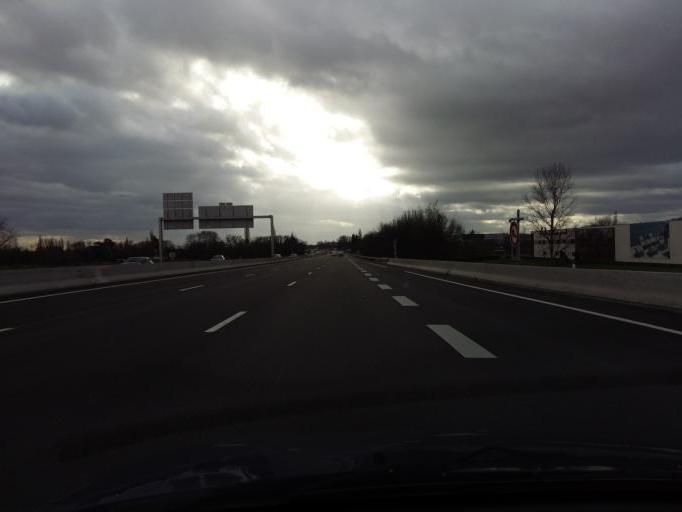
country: FR
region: Bourgogne
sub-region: Departement de Saone-et-Loire
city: Charnay-les-Macon
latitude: 46.2833
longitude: 4.7885
